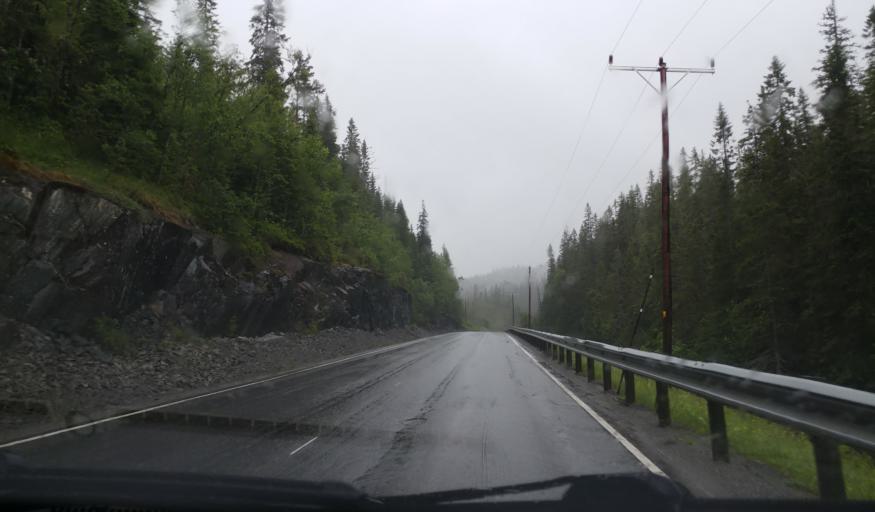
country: NO
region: Sor-Trondelag
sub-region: Selbu
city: Mebonden
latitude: 63.3574
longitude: 11.0769
